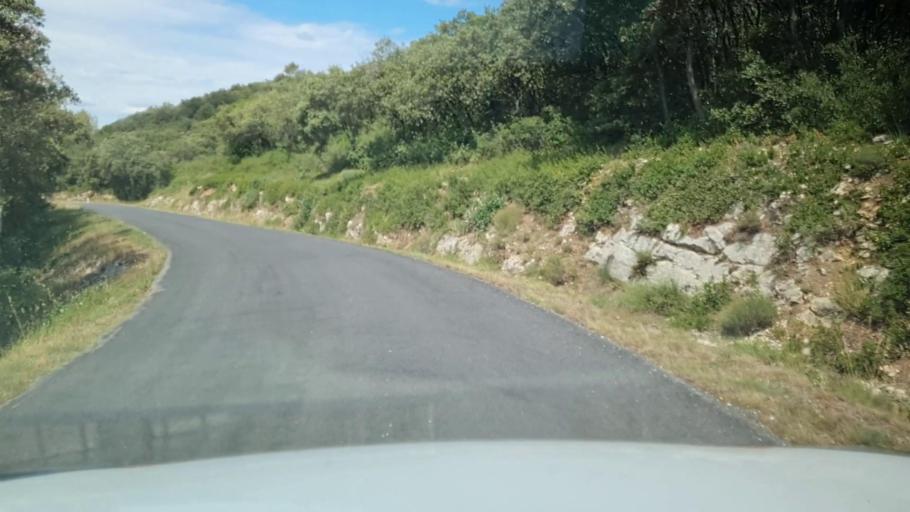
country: FR
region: Languedoc-Roussillon
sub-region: Departement du Gard
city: Calvisson
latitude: 43.8262
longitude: 4.1589
